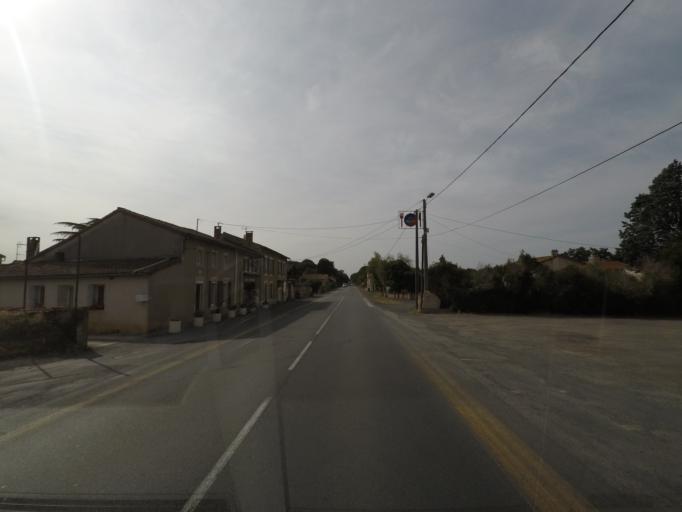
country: FR
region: Poitou-Charentes
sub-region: Departement des Deux-Sevres
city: Lezay
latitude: 46.1767
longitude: -0.0134
